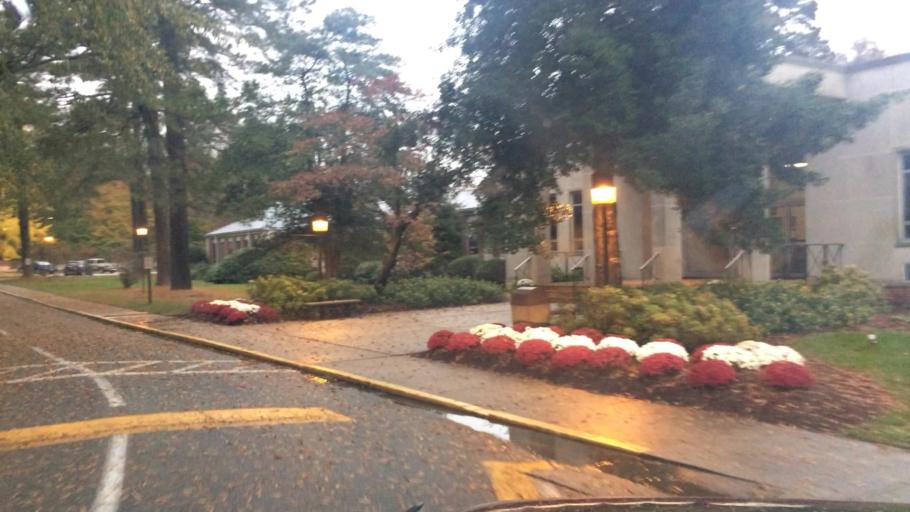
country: US
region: Virginia
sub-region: James City County
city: Williamsburg
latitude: 37.2567
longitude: -76.7265
